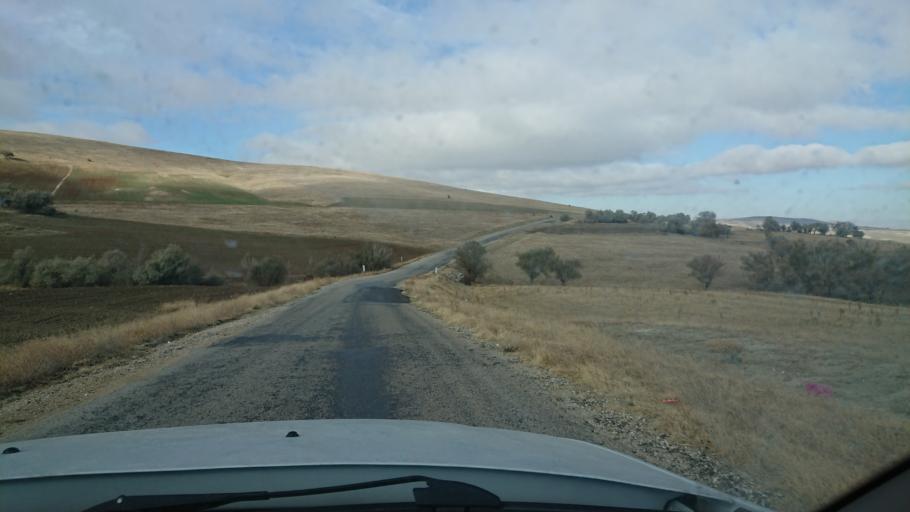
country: TR
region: Aksaray
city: Ortakoy
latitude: 38.7888
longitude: 33.9996
